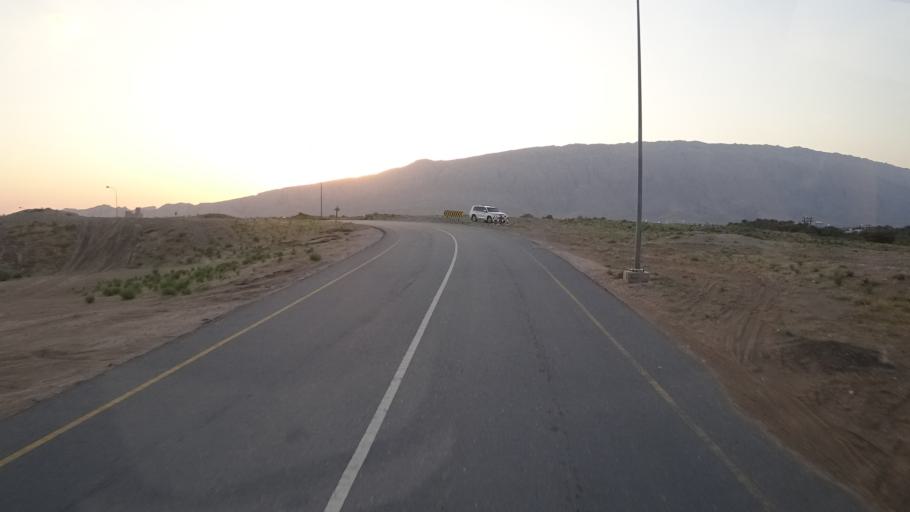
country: AE
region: Abu Dhabi
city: Al Ain
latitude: 23.9841
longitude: 55.8424
